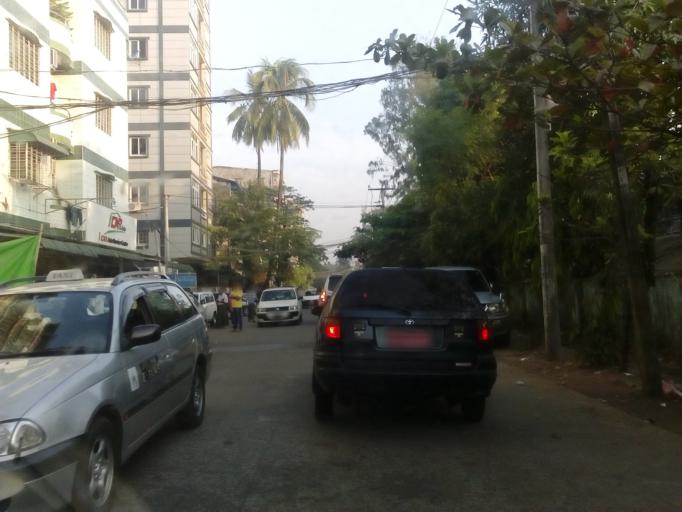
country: MM
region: Yangon
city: Yangon
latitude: 16.8012
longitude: 96.1787
